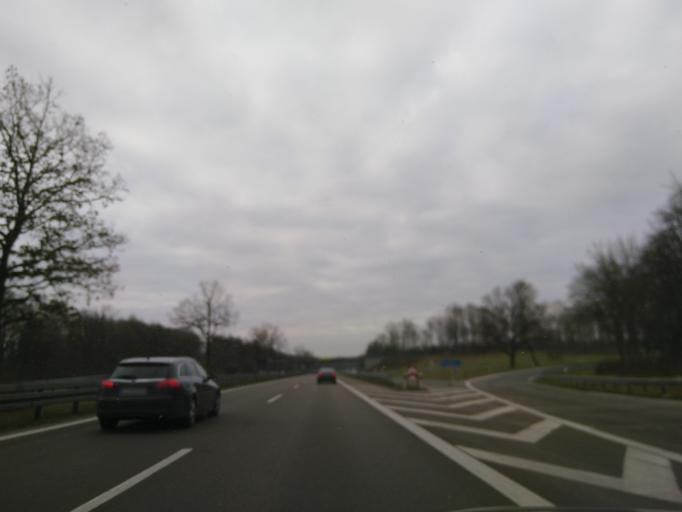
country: DE
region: Bavaria
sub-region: Upper Bavaria
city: Unterhaching
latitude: 48.0851
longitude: 11.5939
